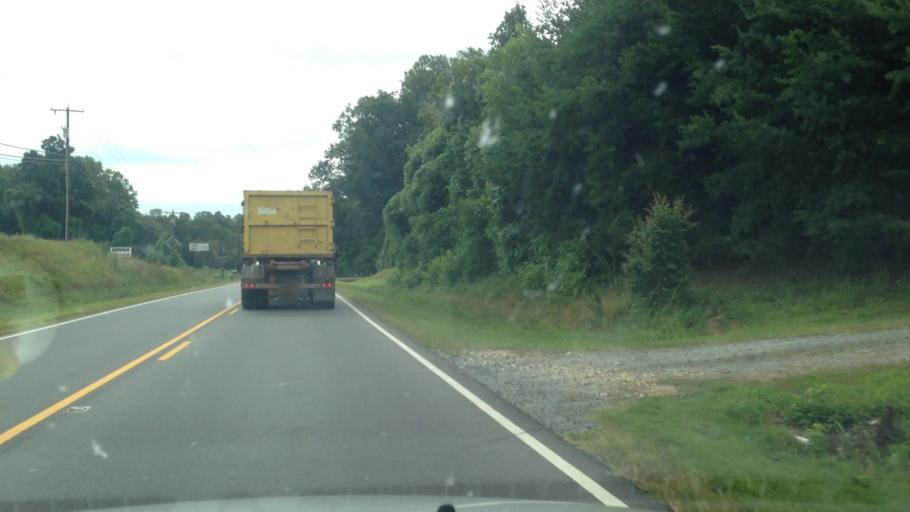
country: US
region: North Carolina
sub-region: Rockingham County
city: Reidsville
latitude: 36.3679
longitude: -79.7192
